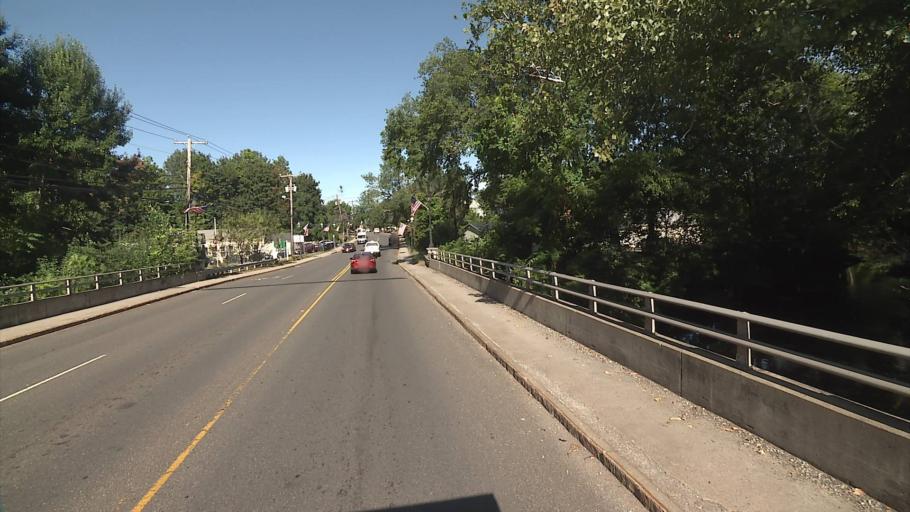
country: US
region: Connecticut
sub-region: New Haven County
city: Meriden
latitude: 41.5182
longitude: -72.8258
